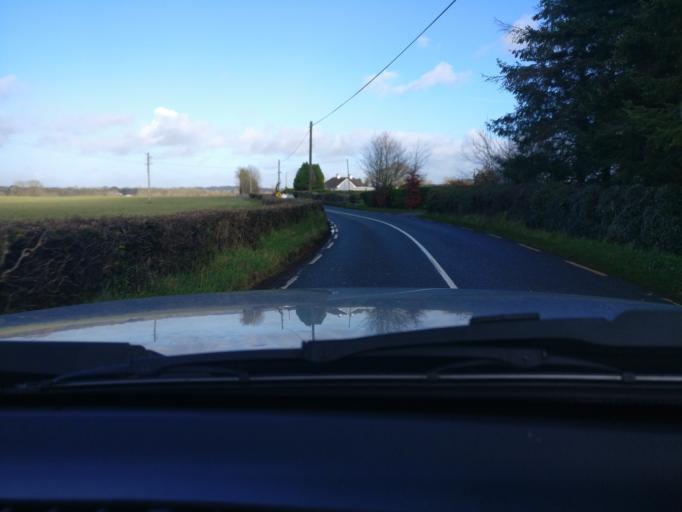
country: IE
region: Leinster
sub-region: An Iarmhi
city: Kilbeggan
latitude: 53.4107
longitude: -7.5681
